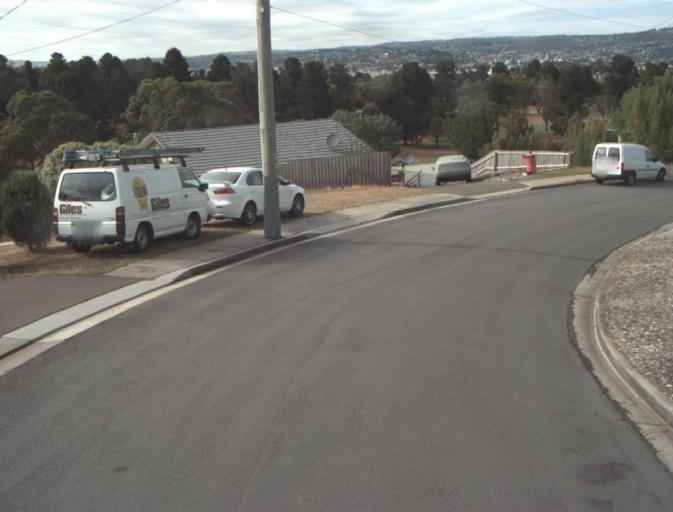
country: AU
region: Tasmania
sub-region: Launceston
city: Invermay
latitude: -41.3910
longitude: 147.1368
